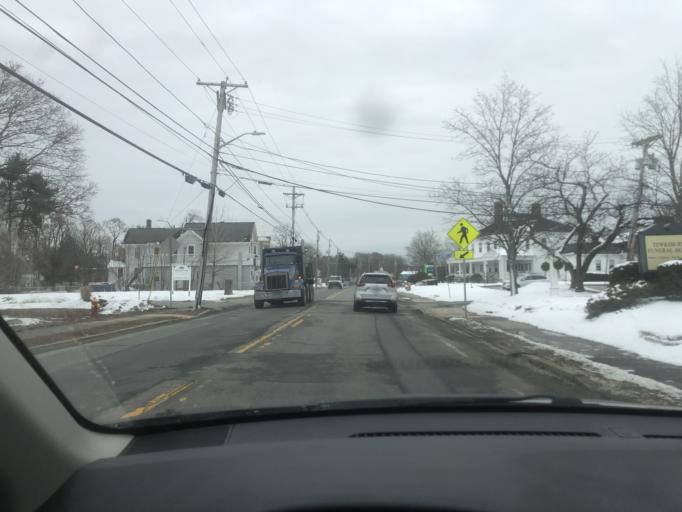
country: US
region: Massachusetts
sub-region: Middlesex County
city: Tewksbury
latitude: 42.6128
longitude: -71.2354
